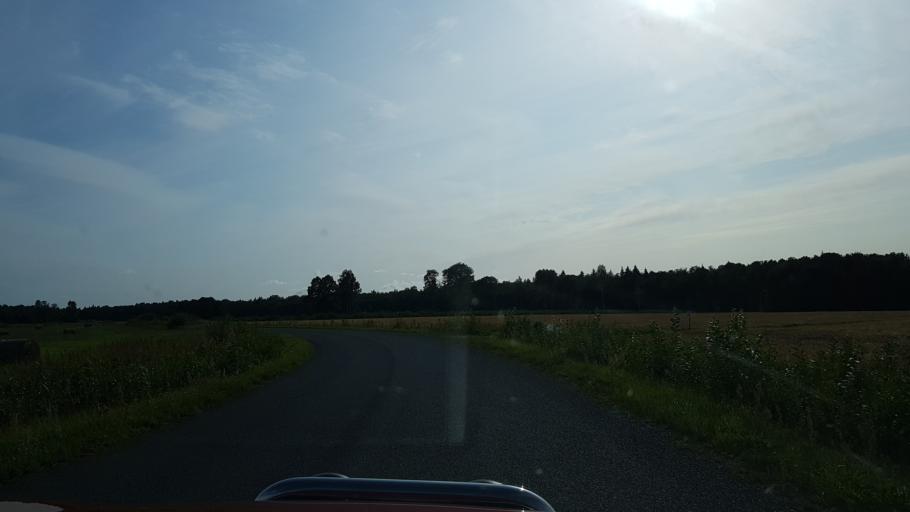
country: EE
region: Laeaene
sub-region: Lihula vald
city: Lihula
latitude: 58.3801
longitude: 24.0015
